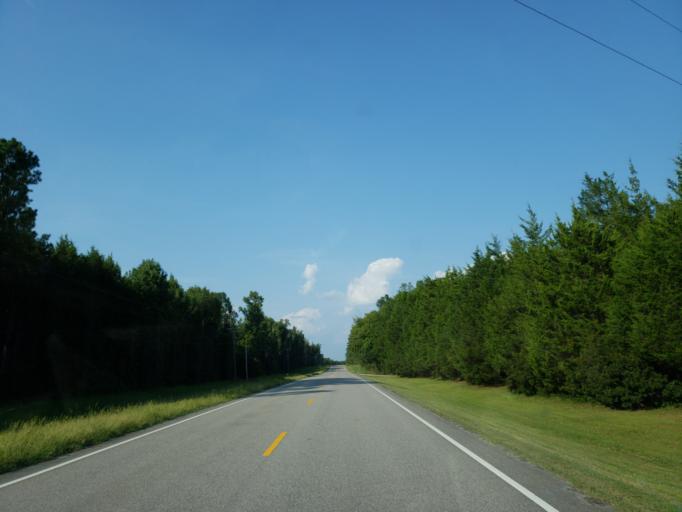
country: US
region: Alabama
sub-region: Greene County
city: Eutaw
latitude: 32.7404
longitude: -88.0510
